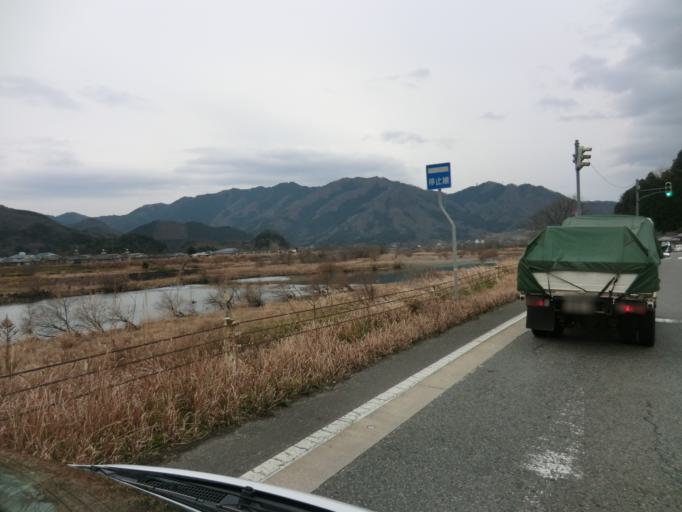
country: JP
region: Hyogo
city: Toyooka
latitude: 35.4351
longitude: 134.7890
